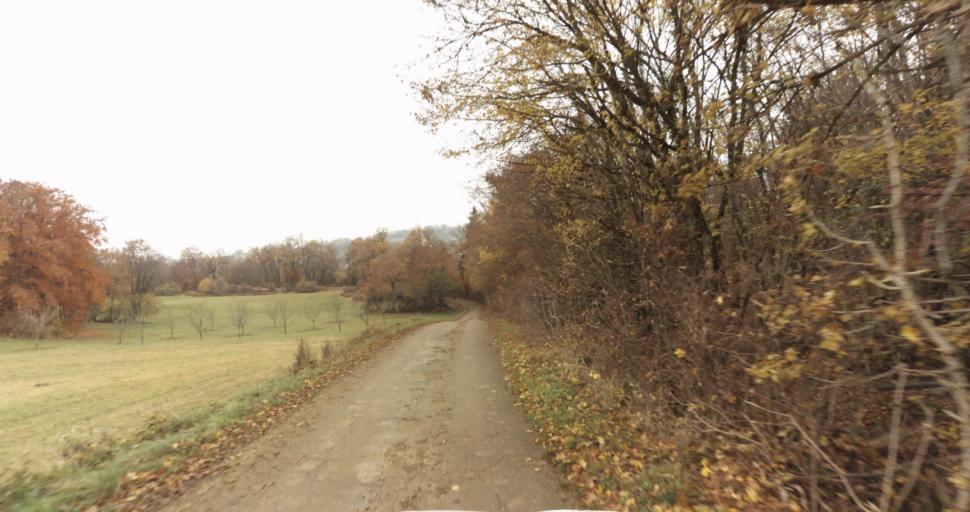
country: FR
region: Rhone-Alpes
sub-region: Departement de la Haute-Savoie
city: Cusy
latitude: 45.7539
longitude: 6.0120
